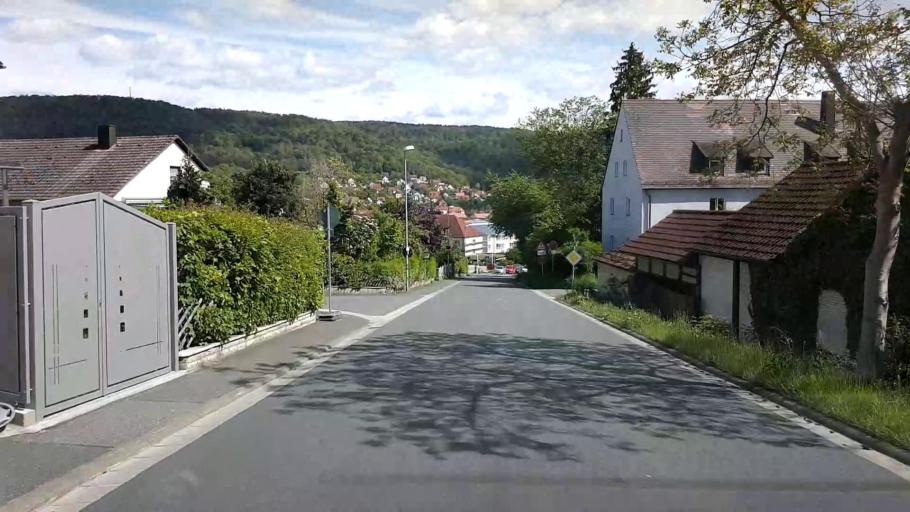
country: DE
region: Bavaria
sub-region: Upper Franconia
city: Ebermannstadt
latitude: 49.7809
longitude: 11.1773
